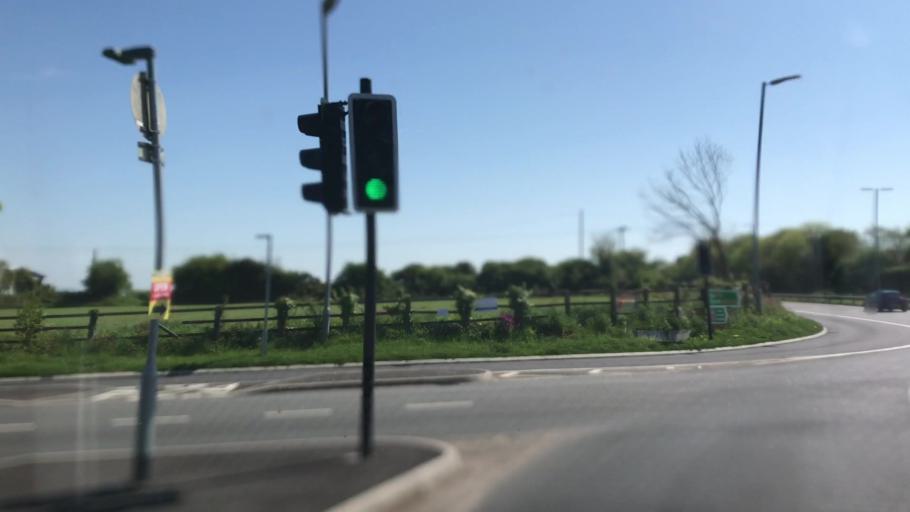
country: GB
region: England
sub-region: Cornwall
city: Chacewater
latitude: 50.2645
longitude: -5.1193
